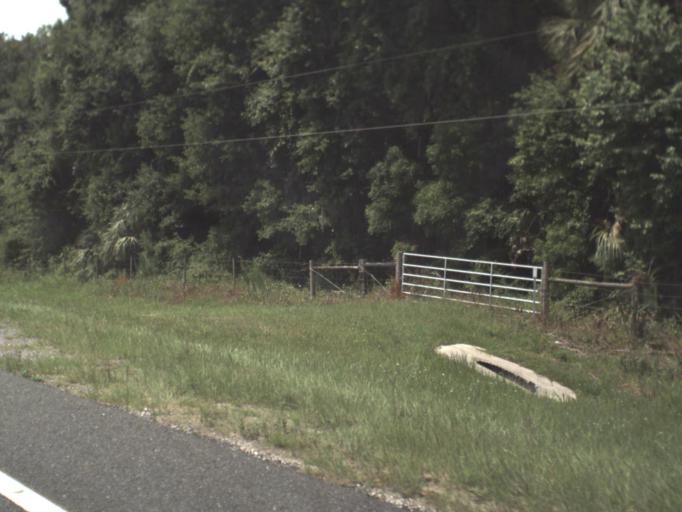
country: US
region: Florida
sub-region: Levy County
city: Chiefland
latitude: 29.4536
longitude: -82.8460
